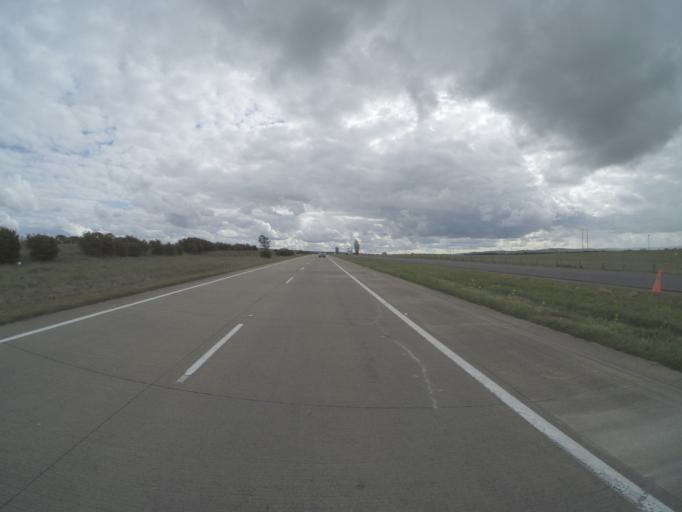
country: AU
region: New South Wales
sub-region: Goulburn Mulwaree
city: Goulburn
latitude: -34.8072
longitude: 149.5425
